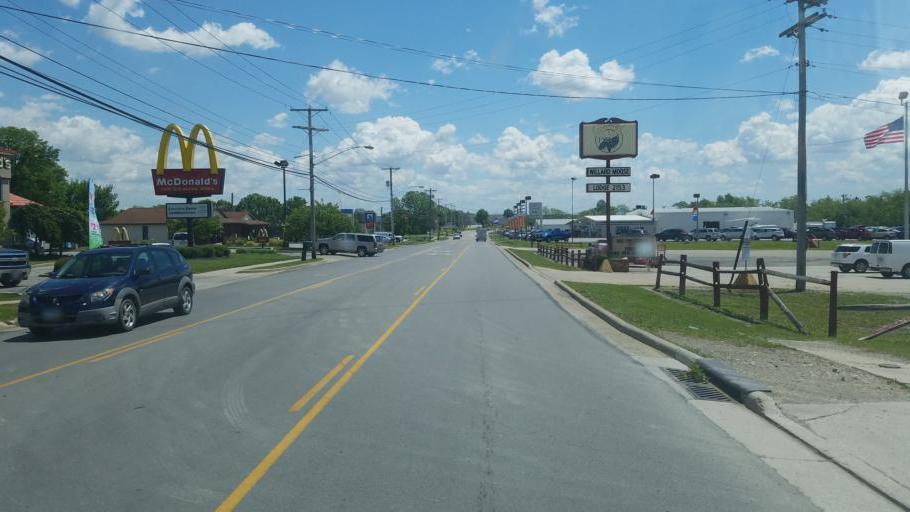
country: US
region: Ohio
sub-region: Huron County
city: Willard
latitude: 41.0427
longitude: -82.7233
